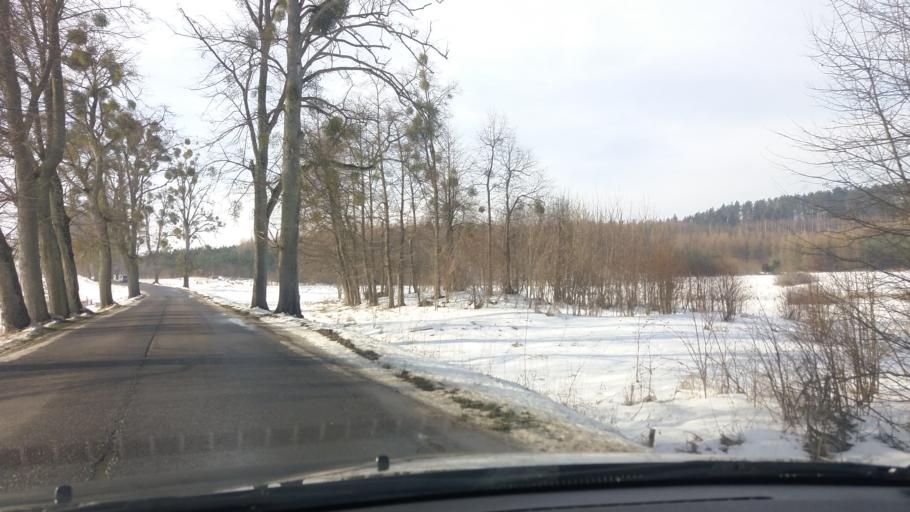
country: PL
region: Warmian-Masurian Voivodeship
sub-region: Powiat lidzbarski
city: Lidzbark Warminski
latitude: 54.1082
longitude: 20.6789
